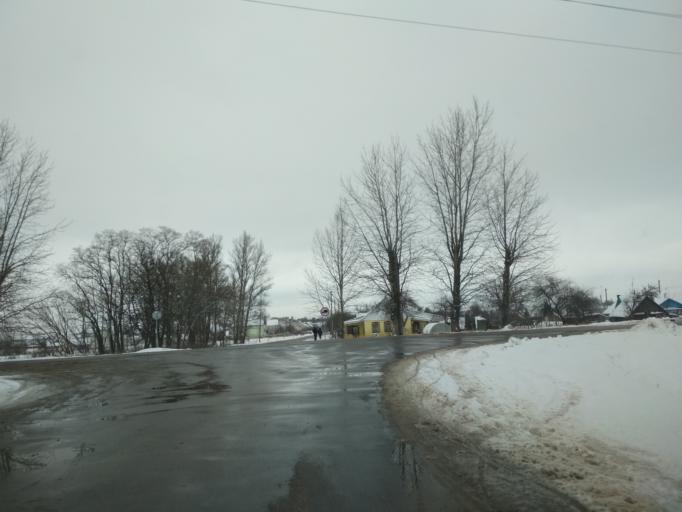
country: BY
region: Minsk
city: Mar''ina Horka
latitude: 53.4938
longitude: 28.1429
